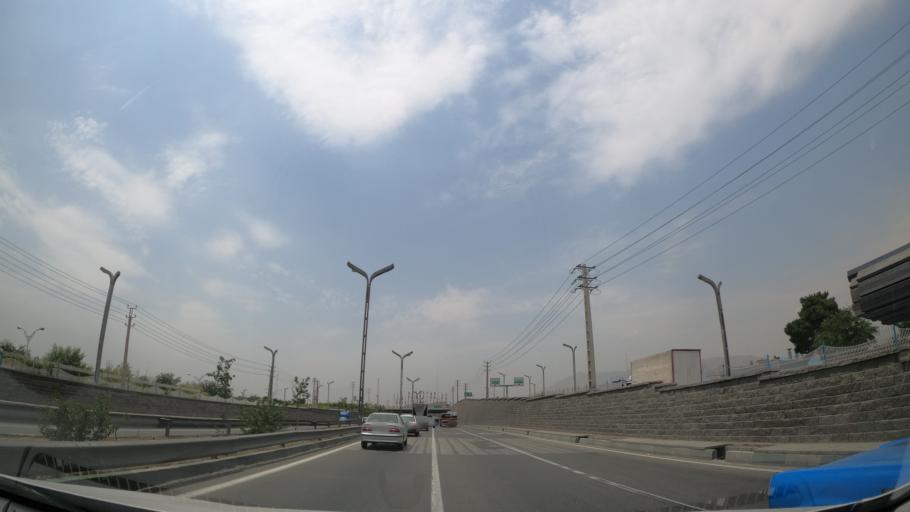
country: IR
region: Tehran
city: Shahr-e Qods
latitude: 35.7025
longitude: 51.1859
